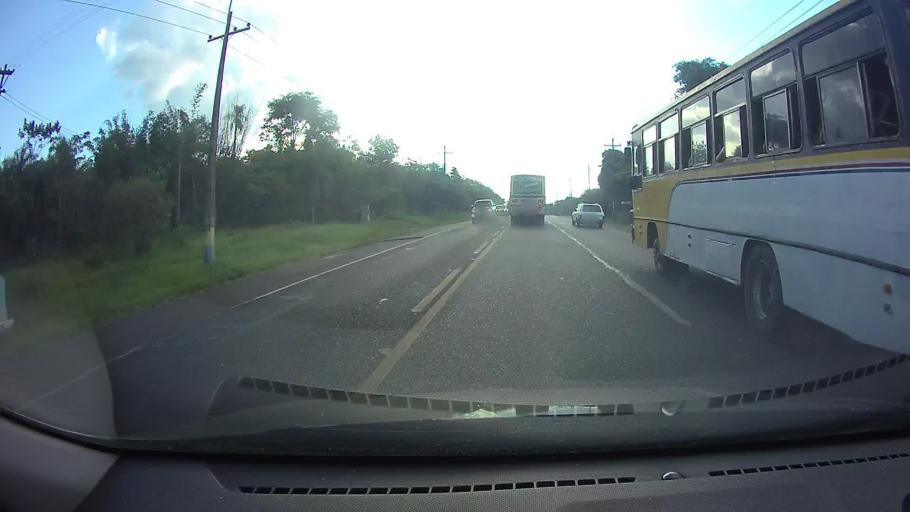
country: PY
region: Cordillera
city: Caacupe
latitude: -25.3881
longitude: -57.0882
